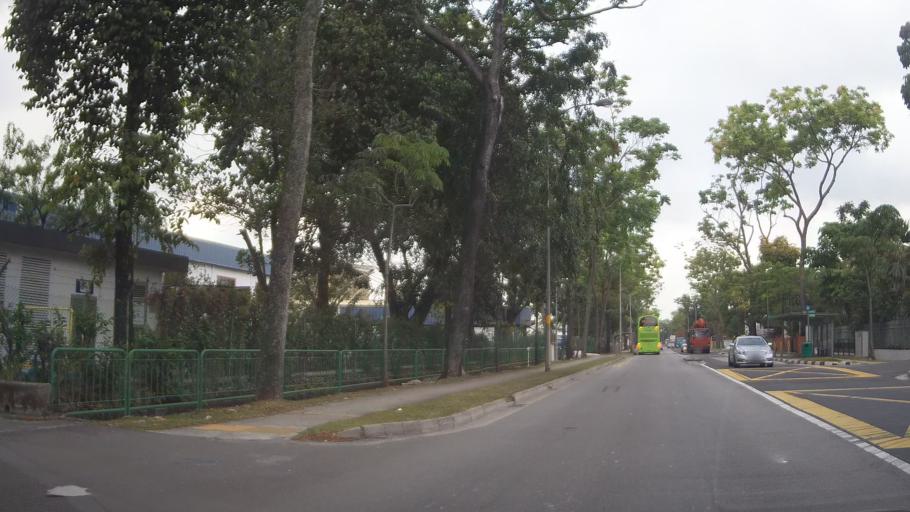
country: MY
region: Johor
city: Johor Bahru
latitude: 1.3181
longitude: 103.6476
